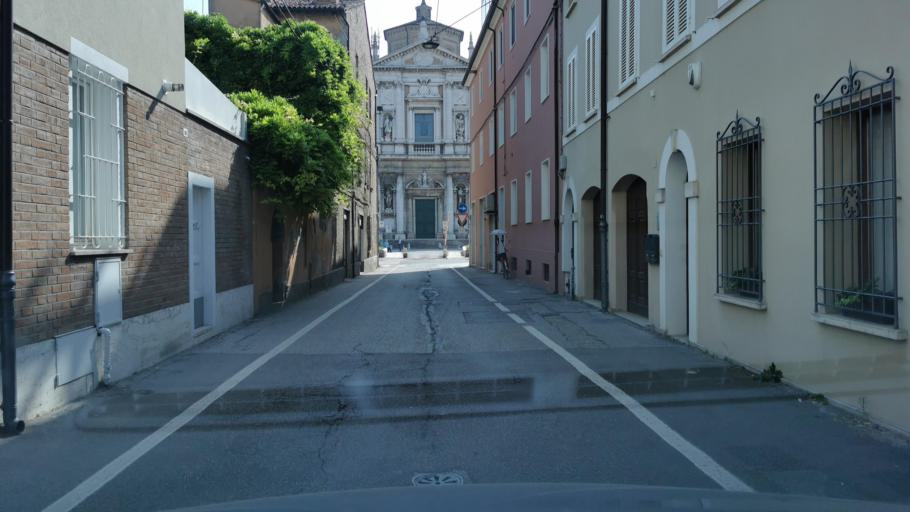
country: IT
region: Emilia-Romagna
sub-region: Provincia di Ravenna
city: Ravenna
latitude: 44.4140
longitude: 12.2049
